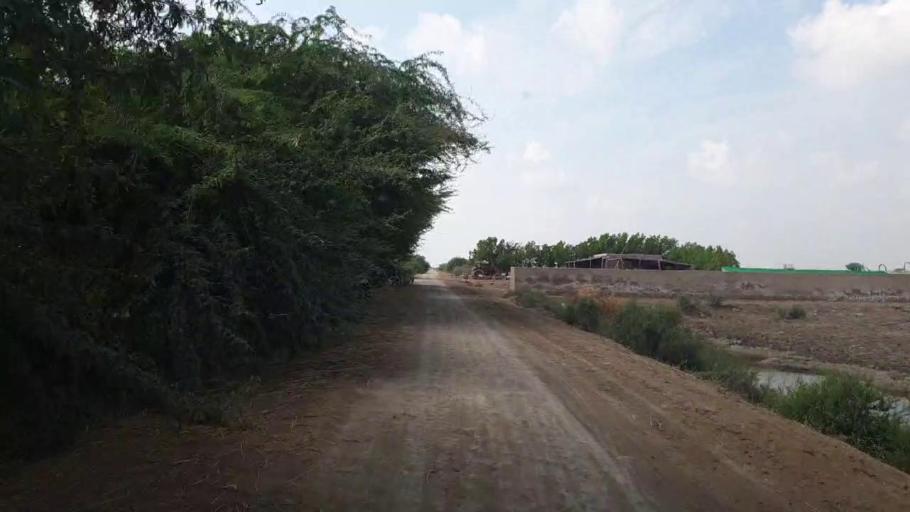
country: PK
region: Sindh
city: Badin
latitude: 24.5065
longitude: 68.6402
